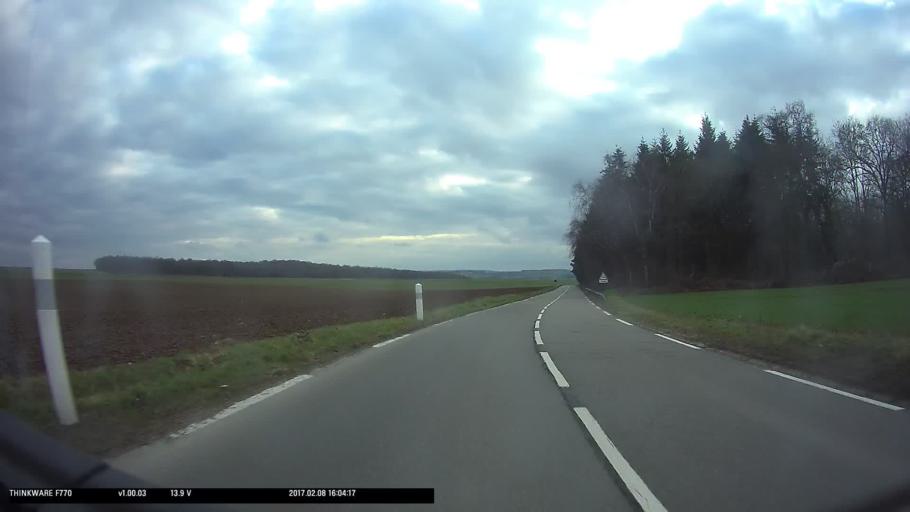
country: FR
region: Ile-de-France
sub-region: Departement du Val-d'Oise
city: Us
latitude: 49.1149
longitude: 1.9818
